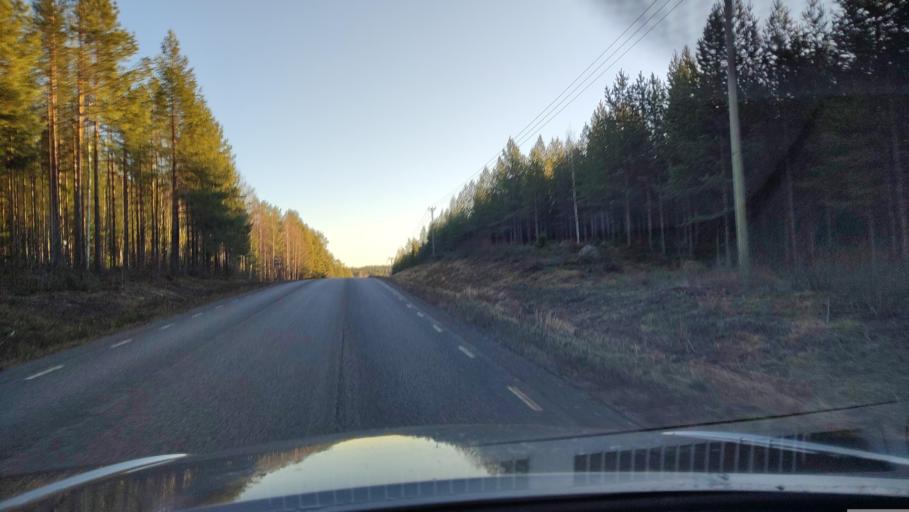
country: SE
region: Vaesterbotten
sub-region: Skelleftea Kommun
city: Viken
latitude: 64.6949
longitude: 20.9297
